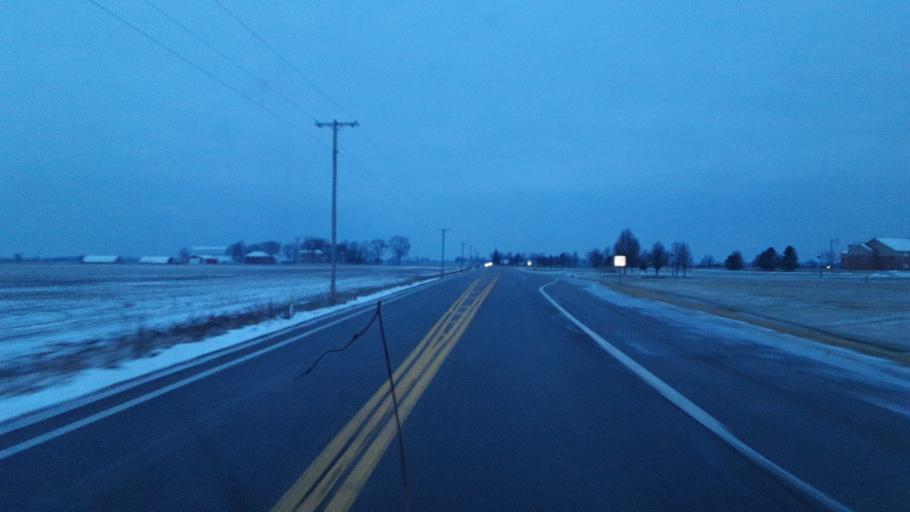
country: US
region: Ohio
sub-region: Marion County
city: Marion
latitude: 40.5826
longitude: -83.0096
